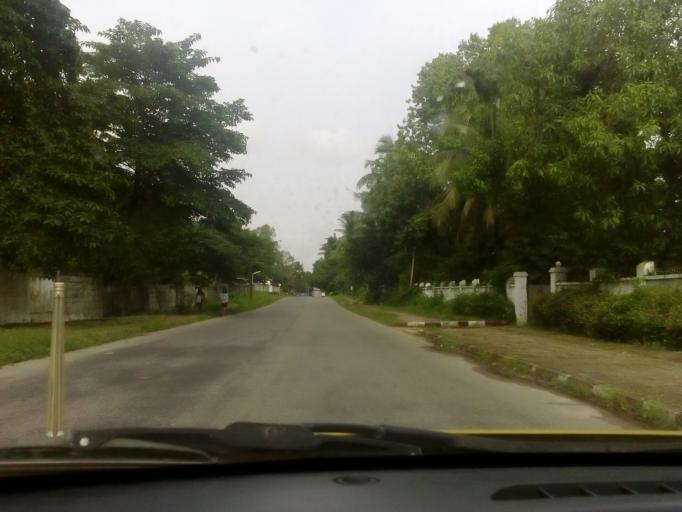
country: MM
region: Yangon
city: Yangon
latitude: 16.8429
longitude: 96.1531
